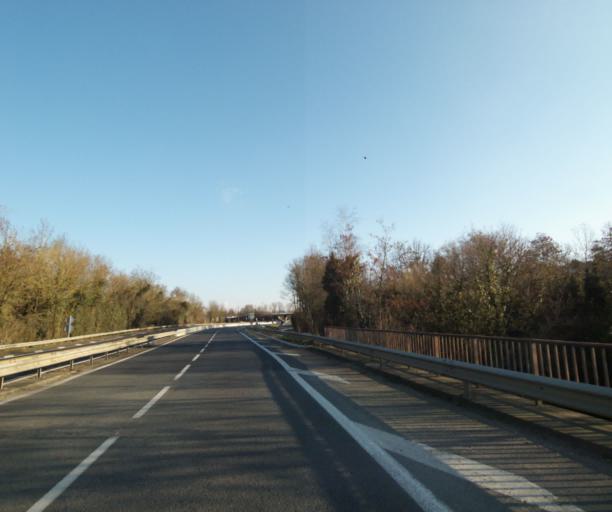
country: FR
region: Poitou-Charentes
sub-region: Departement des Deux-Sevres
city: Niort
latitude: 46.3347
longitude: -0.4653
